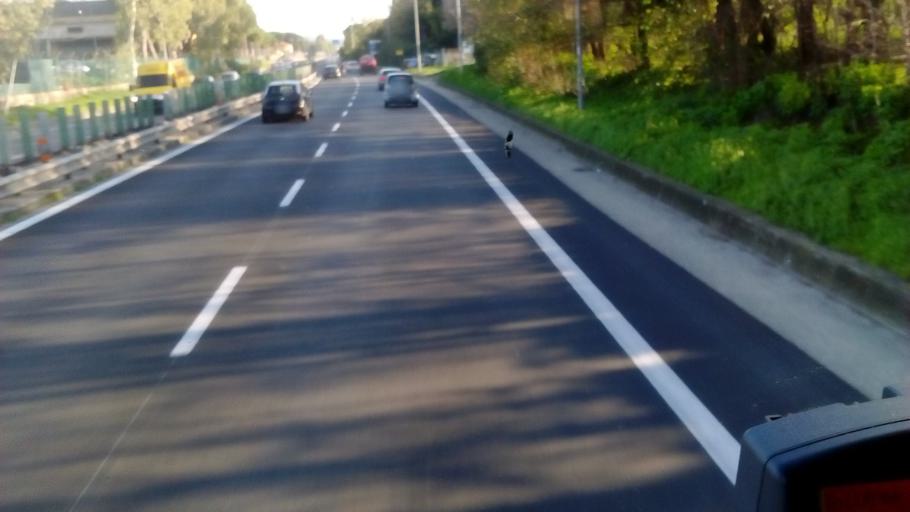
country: IT
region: Latium
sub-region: Citta metropolitana di Roma Capitale
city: Ciampino
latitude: 41.7927
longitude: 12.5920
